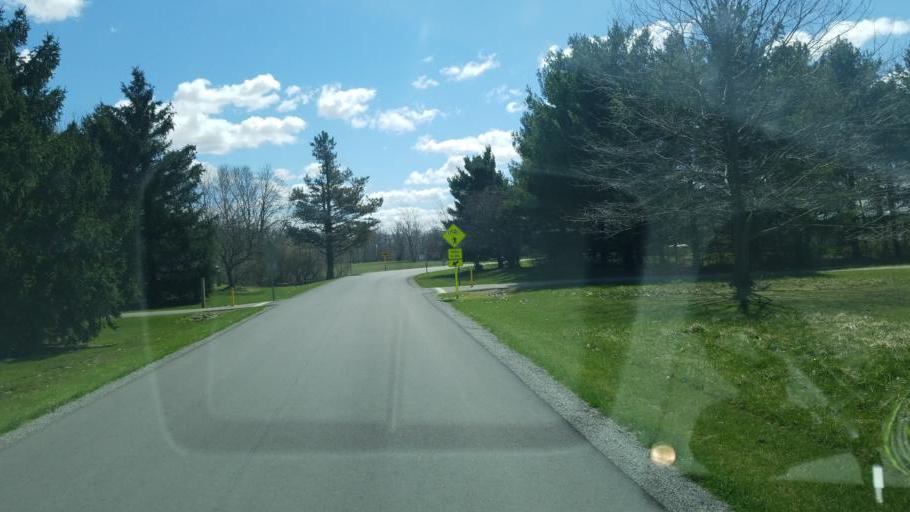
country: US
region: Ohio
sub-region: Hancock County
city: Findlay
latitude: 41.0294
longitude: -83.5599
